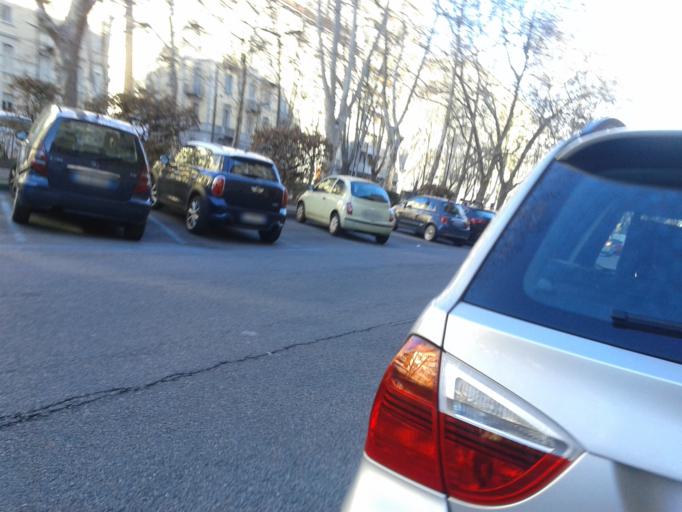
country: IT
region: Piedmont
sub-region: Provincia di Torino
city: Turin
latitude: 45.0590
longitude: 7.6605
